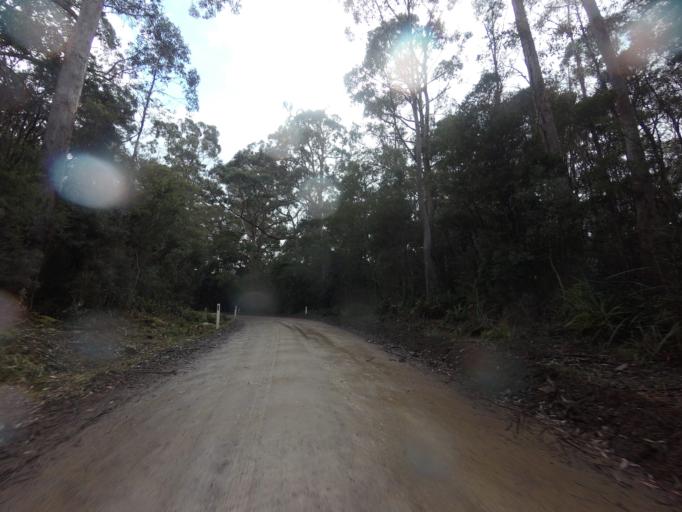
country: AU
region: Tasmania
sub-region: Huon Valley
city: Geeveston
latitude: -43.5765
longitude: 146.8880
